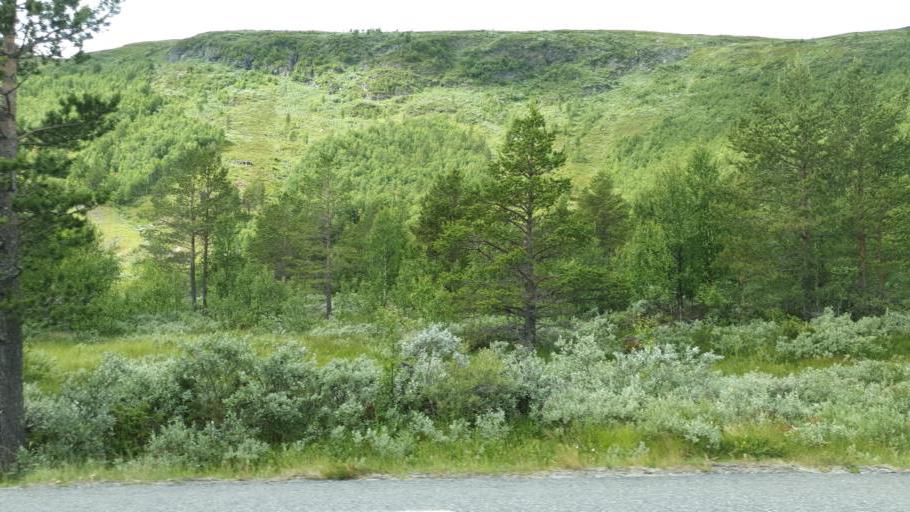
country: NO
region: Oppland
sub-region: Vaga
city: Vagamo
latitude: 61.7567
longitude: 9.0707
